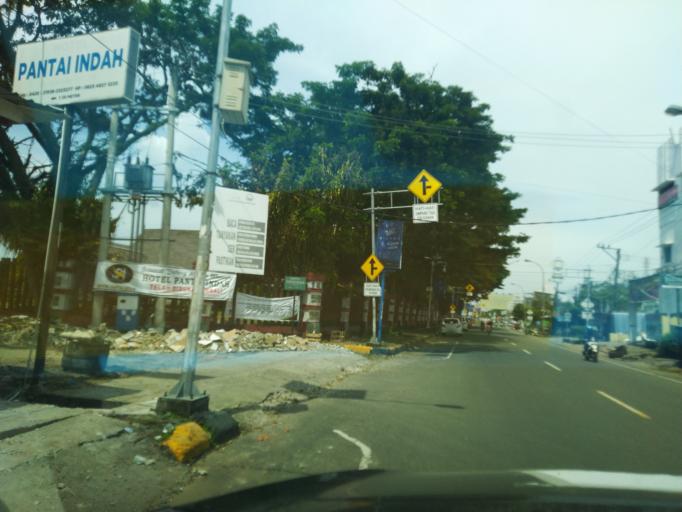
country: ID
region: Sulawesi Barat
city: Mamuju
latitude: -2.6769
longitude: 118.8840
